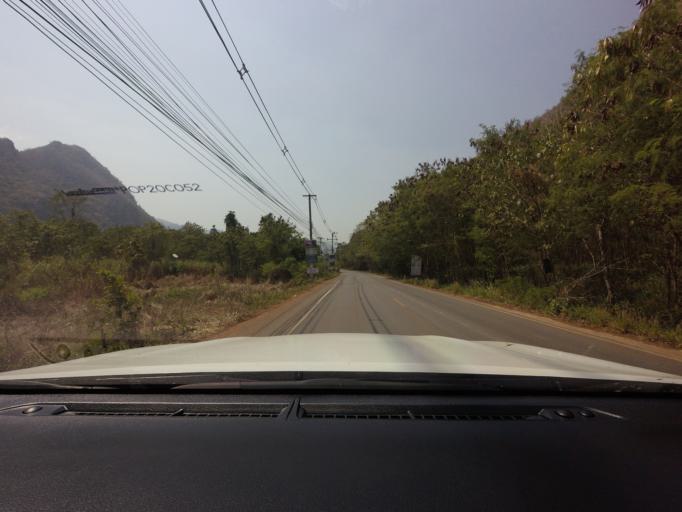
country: TH
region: Nakhon Ratchasima
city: Pak Chong
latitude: 14.5413
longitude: 101.3507
